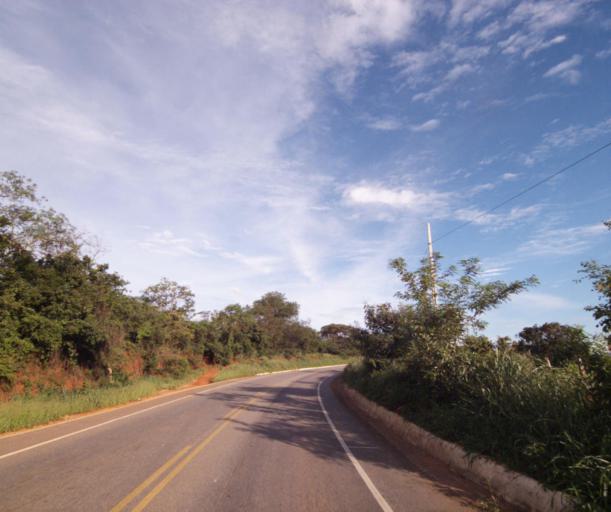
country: BR
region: Bahia
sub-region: Caetite
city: Caetite
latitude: -14.0705
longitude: -42.4601
